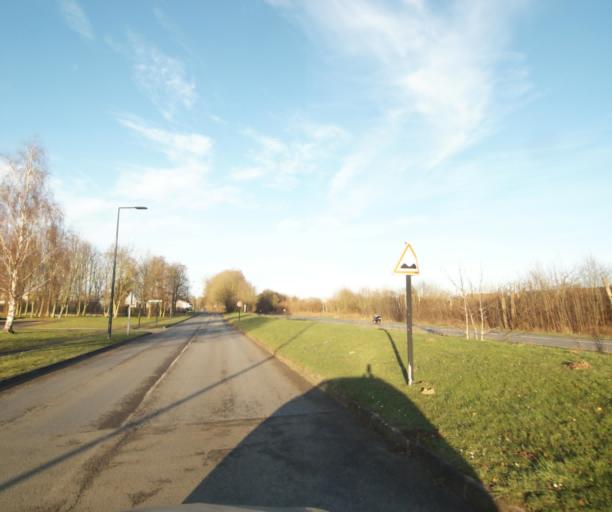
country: FR
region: Nord-Pas-de-Calais
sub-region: Departement du Nord
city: Famars
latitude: 50.3228
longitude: 3.5159
